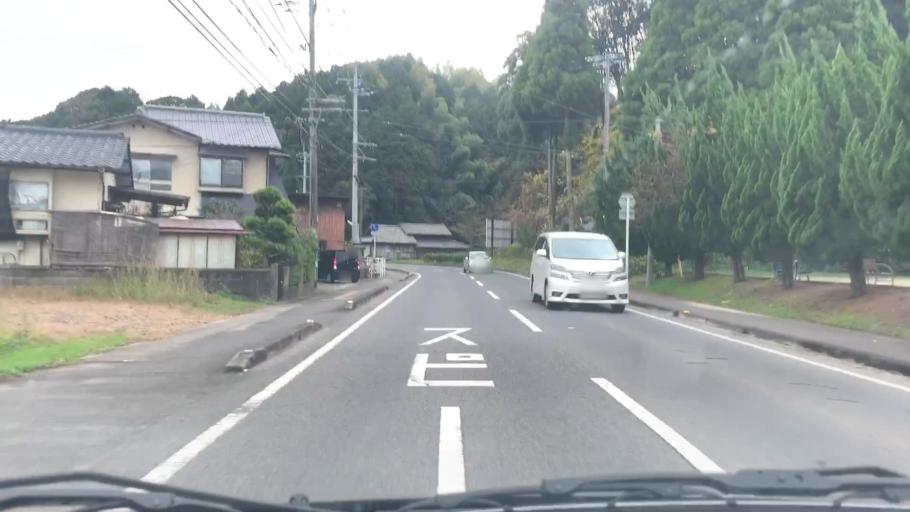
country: JP
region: Saga Prefecture
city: Takeocho-takeo
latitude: 33.1920
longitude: 130.0319
